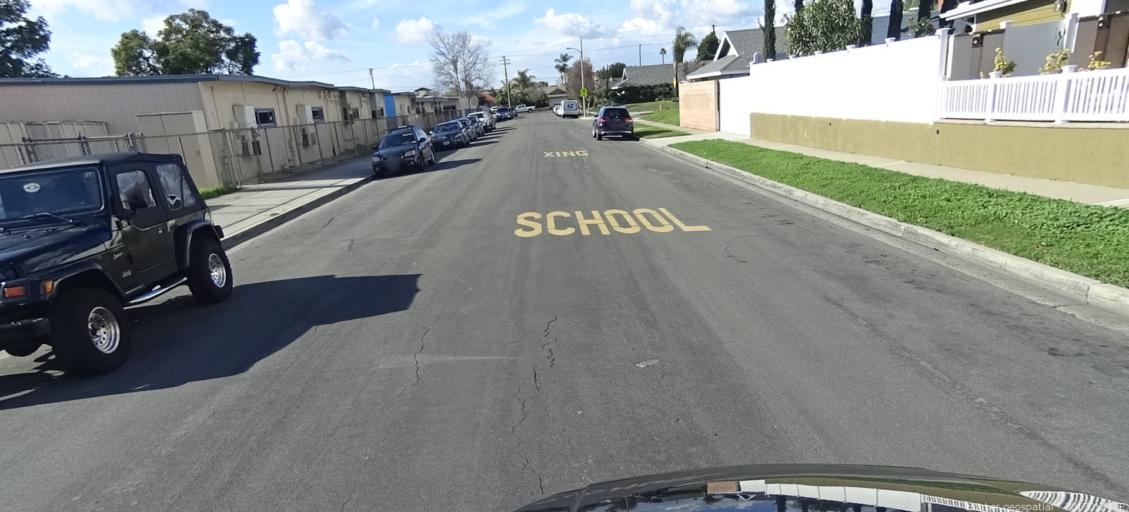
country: US
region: California
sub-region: Orange County
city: Laguna Hills
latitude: 33.6161
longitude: -117.6966
